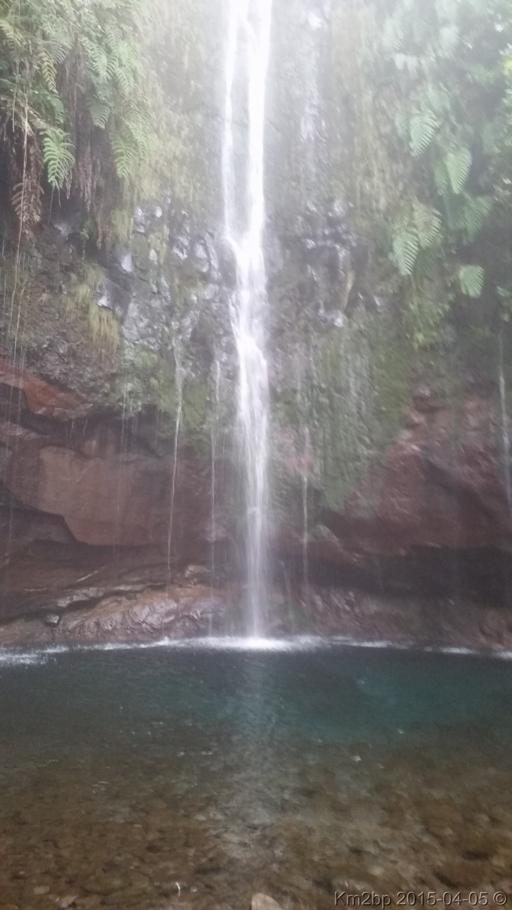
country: PT
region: Madeira
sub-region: Calheta
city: Arco da Calheta
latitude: 32.7655
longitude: -17.1255
